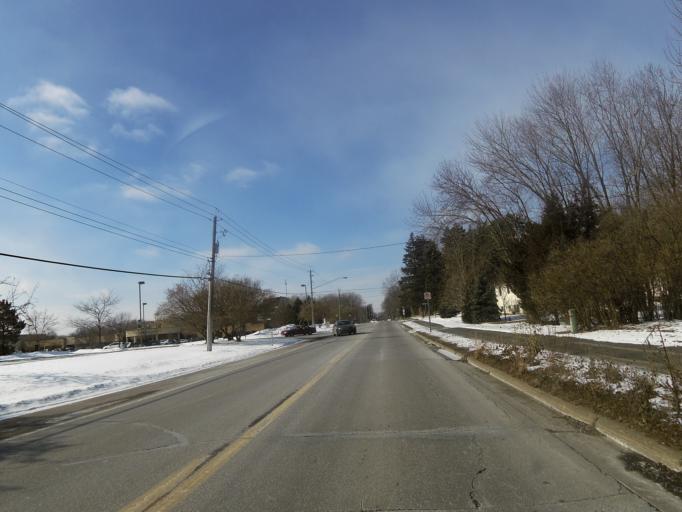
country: US
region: Minnesota
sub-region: Washington County
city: Oakdale
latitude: 44.9705
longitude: -92.9805
